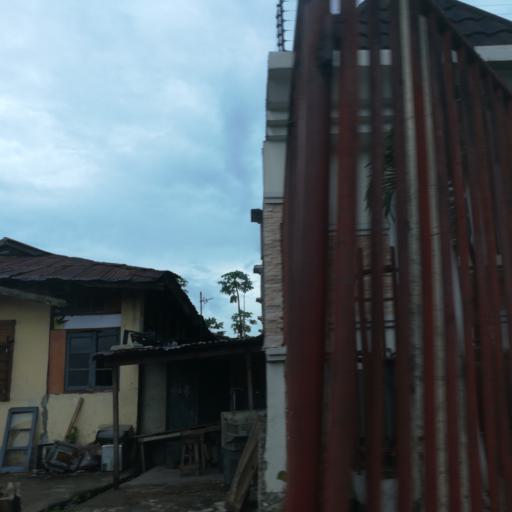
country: NG
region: Lagos
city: Makoko
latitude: 6.5017
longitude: 3.3767
